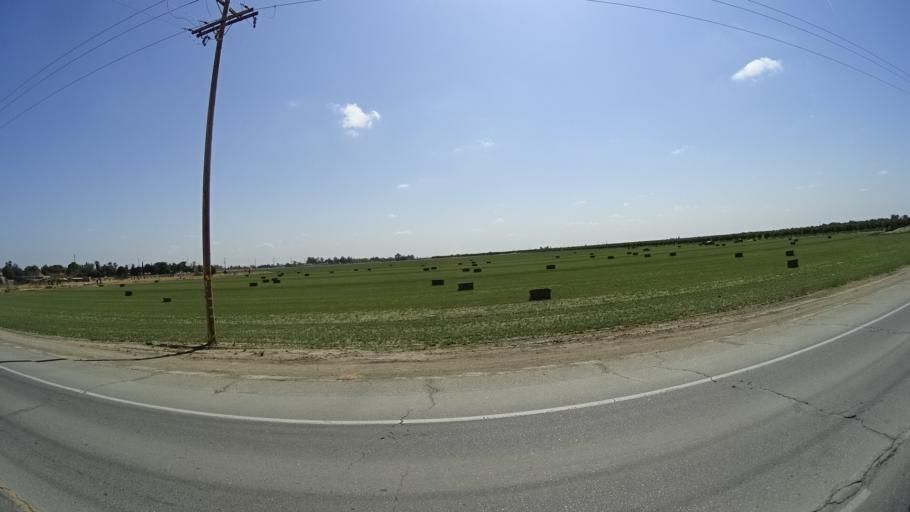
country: US
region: California
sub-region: Kings County
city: Home Garden
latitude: 36.2962
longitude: -119.6370
